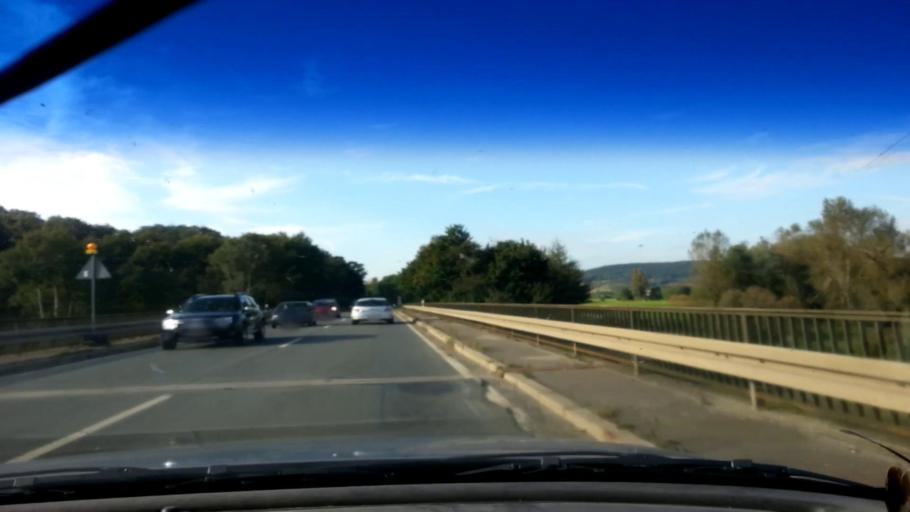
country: DE
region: Bavaria
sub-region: Upper Franconia
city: Baunach
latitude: 49.9787
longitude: 10.8593
